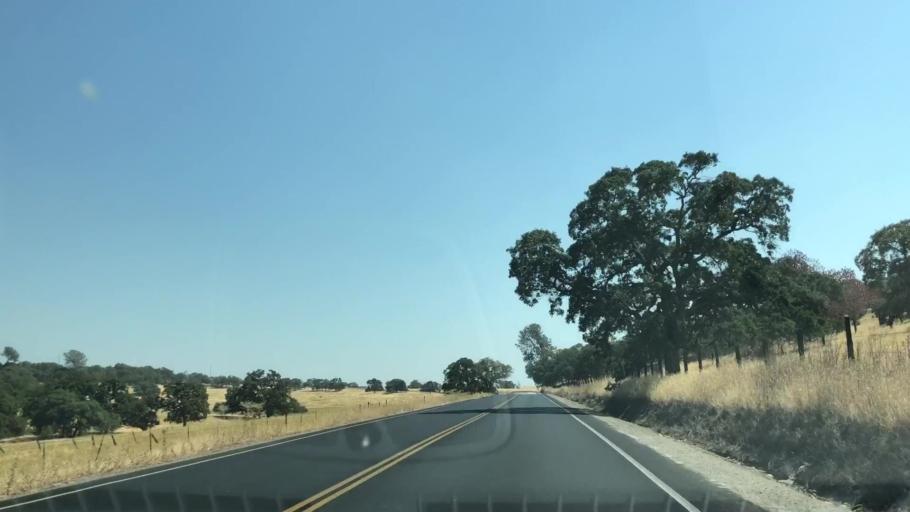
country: US
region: California
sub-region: Tuolumne County
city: Jamestown
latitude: 37.8851
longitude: -120.4833
